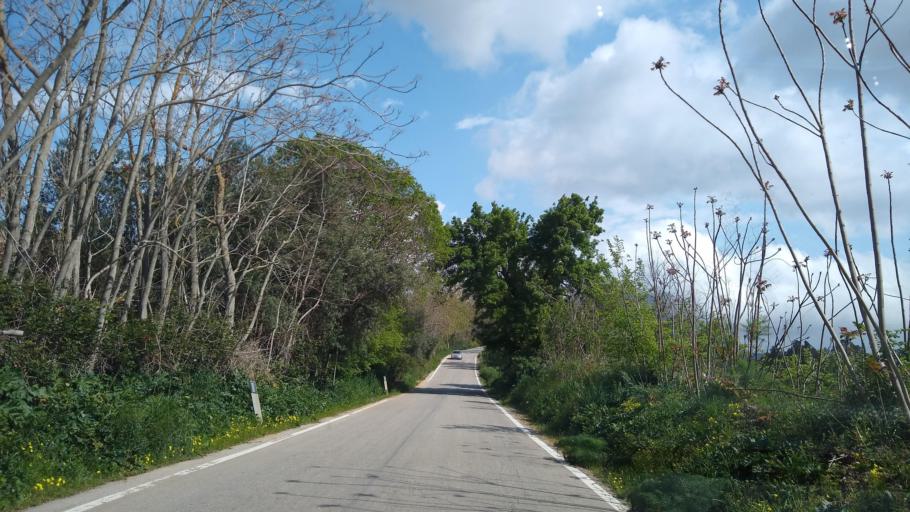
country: IT
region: Sicily
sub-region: Trapani
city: Calatafimi
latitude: 37.9376
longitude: 12.8506
